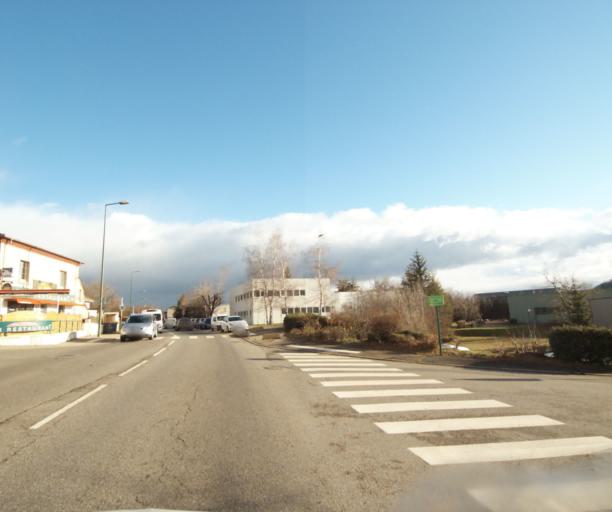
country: FR
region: Rhone-Alpes
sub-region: Departement de la Loire
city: La Talaudiere
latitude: 45.4642
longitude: 4.4197
